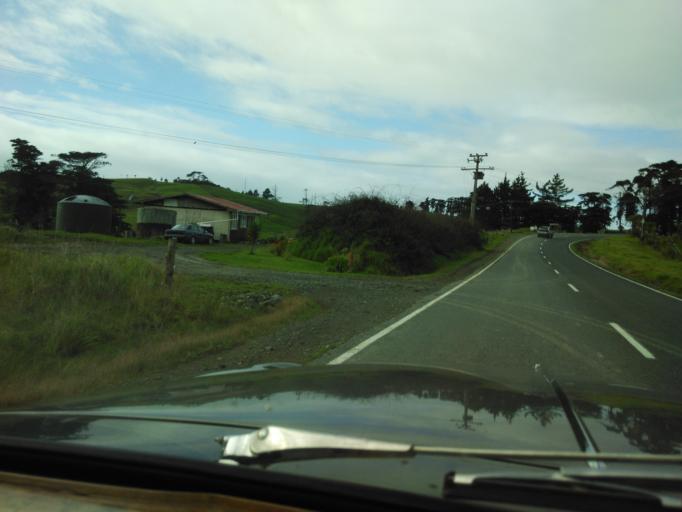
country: NZ
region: Auckland
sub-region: Auckland
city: Wellsford
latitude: -36.3319
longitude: 174.3927
